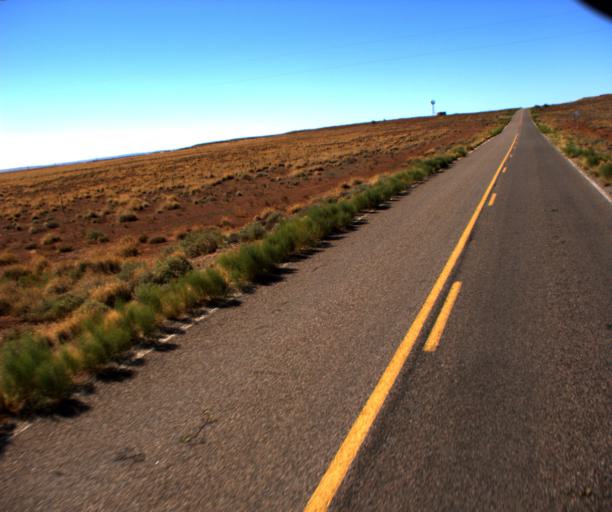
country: US
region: Arizona
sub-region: Coconino County
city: LeChee
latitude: 35.2465
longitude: -110.9610
